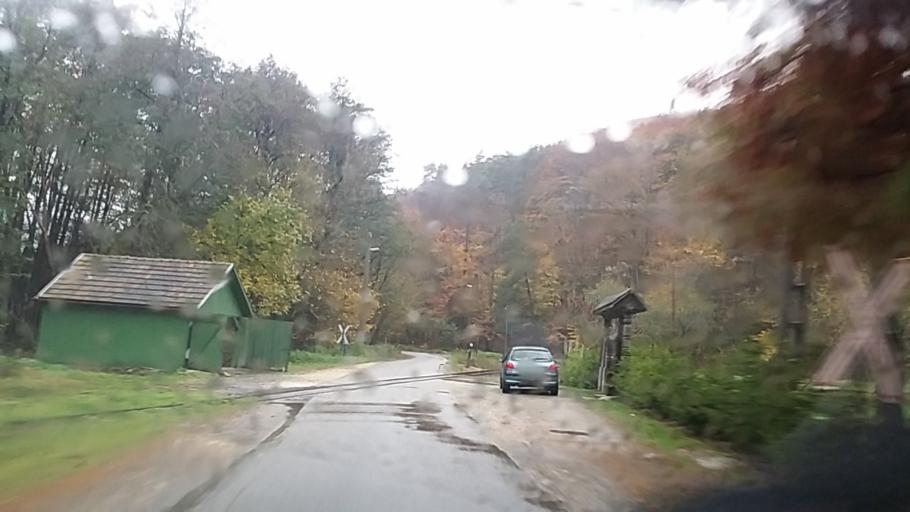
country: HU
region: Borsod-Abauj-Zemplen
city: Tolcsva
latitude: 48.4475
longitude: 21.4627
